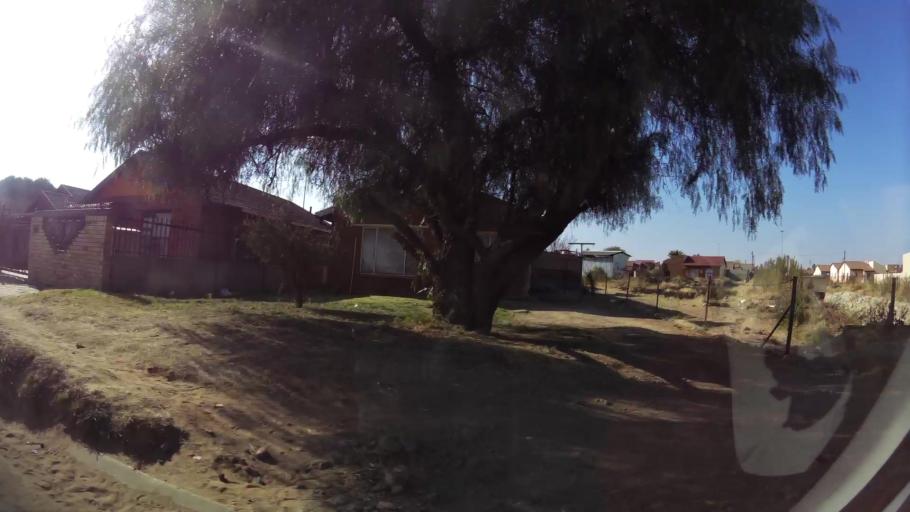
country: ZA
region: Orange Free State
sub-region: Mangaung Metropolitan Municipality
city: Bloemfontein
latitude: -29.1828
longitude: 26.2235
